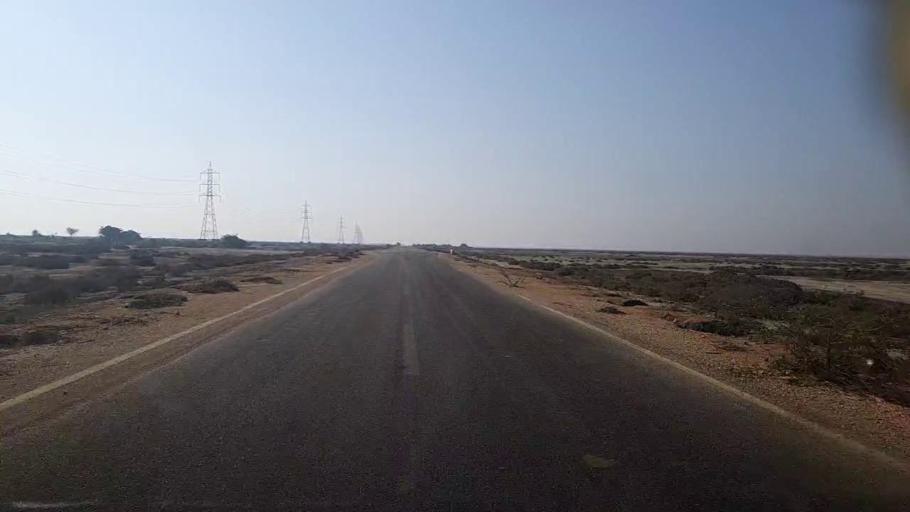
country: PK
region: Sindh
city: Gharo
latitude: 24.6226
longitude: 67.4969
